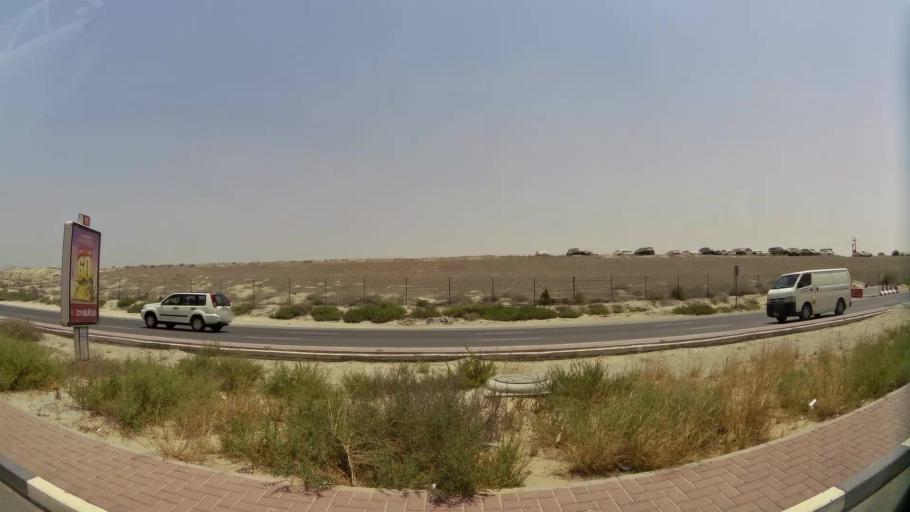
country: AE
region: Ash Shariqah
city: Sharjah
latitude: 25.2808
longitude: 55.4145
